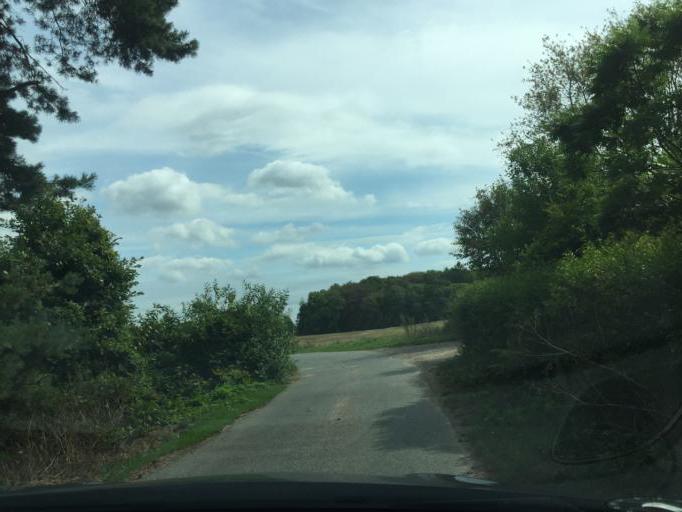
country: DK
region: South Denmark
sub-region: Nordfyns Kommune
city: Sonderso
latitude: 55.4144
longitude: 10.2184
